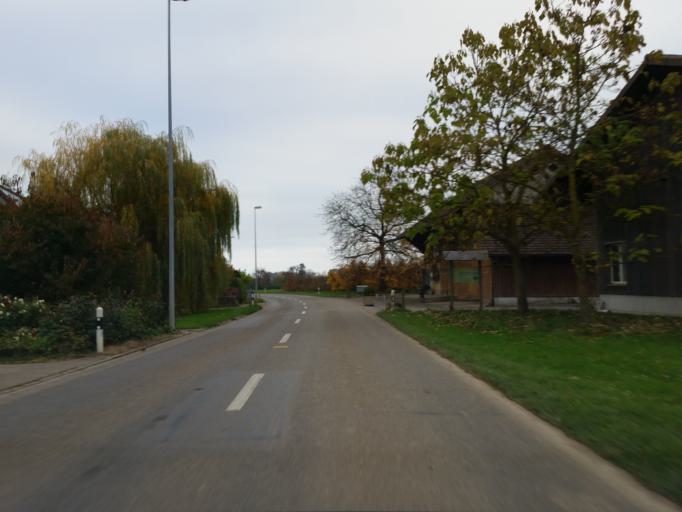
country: CH
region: Thurgau
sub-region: Arbon District
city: Salmsach
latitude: 47.5488
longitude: 9.3511
